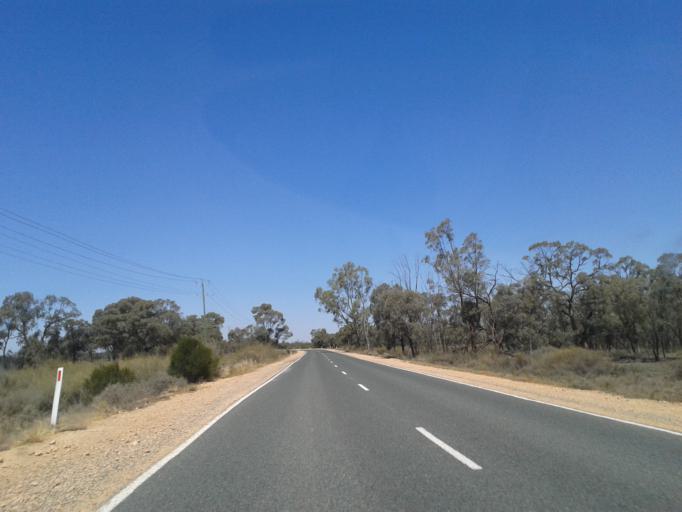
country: AU
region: Victoria
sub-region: Mildura Shire
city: Ouyen
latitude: -34.7024
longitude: 142.8823
